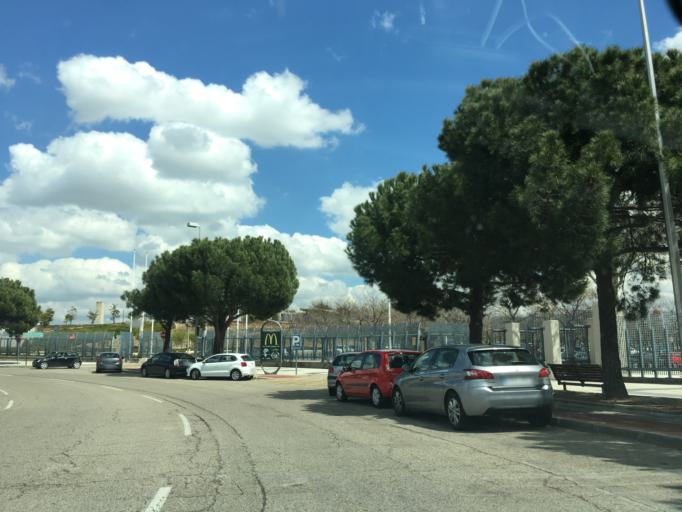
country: ES
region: Madrid
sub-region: Provincia de Madrid
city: San Blas
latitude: 40.4600
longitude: -3.6153
